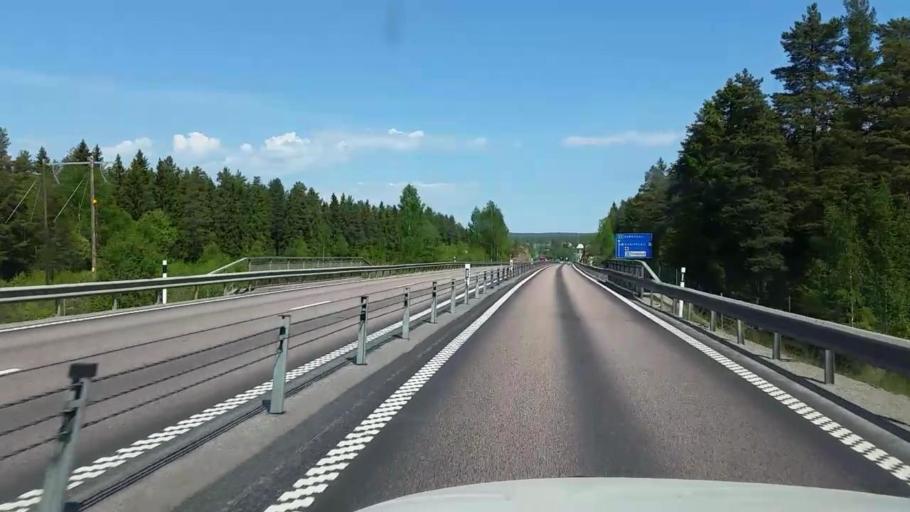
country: SE
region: Gaevleborg
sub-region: Hudiksvalls Kommun
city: Hudiksvall
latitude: 61.7388
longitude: 17.0717
